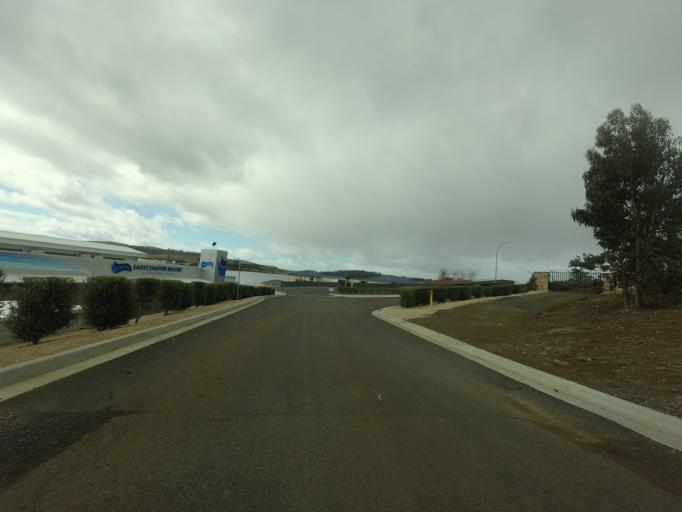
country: AU
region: Tasmania
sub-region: Sorell
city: Sorell
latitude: -42.5426
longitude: 147.9130
